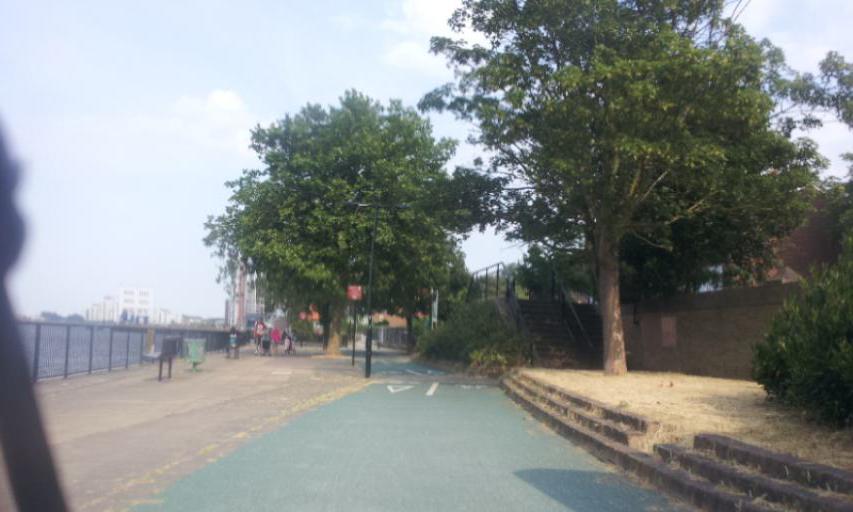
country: GB
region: England
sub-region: Greater London
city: Woolwich
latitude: 51.4945
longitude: 0.0546
